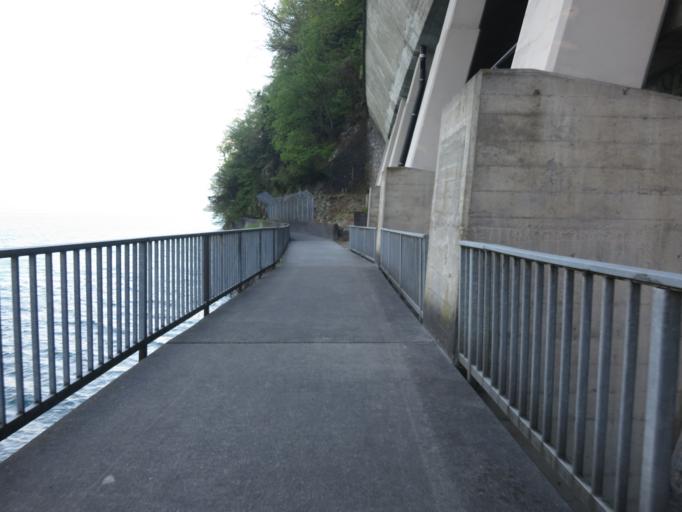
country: CH
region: Saint Gallen
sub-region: Wahlkreis See-Gaster
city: Amden
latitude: 47.1253
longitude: 9.1390
